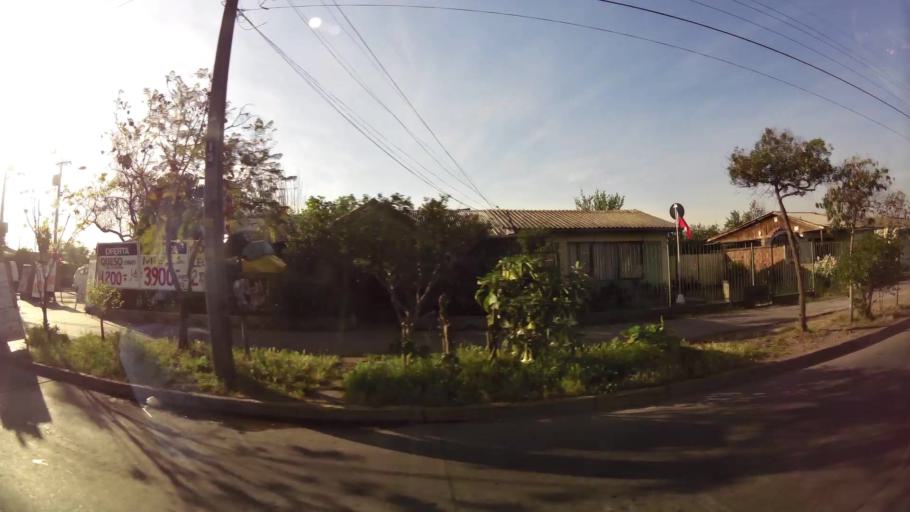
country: CL
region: Santiago Metropolitan
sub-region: Provincia de Santiago
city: Villa Presidente Frei, Nunoa, Santiago, Chile
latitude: -33.5133
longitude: -70.6159
